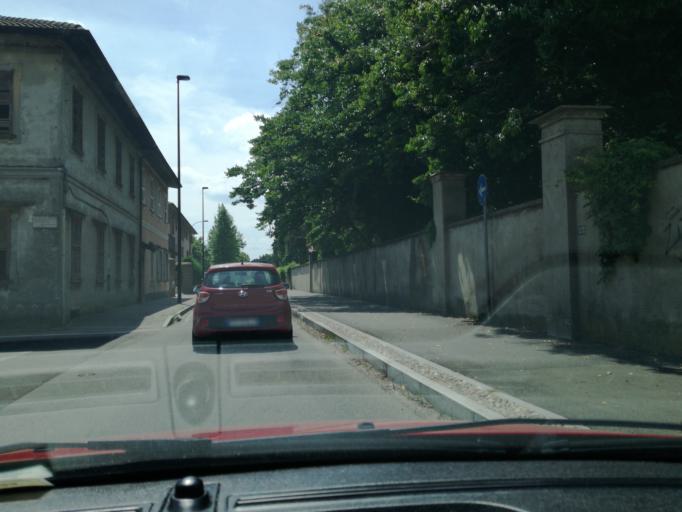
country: IT
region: Lombardy
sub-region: Provincia di Monza e Brianza
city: Limbiate
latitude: 45.6131
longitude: 9.1324
